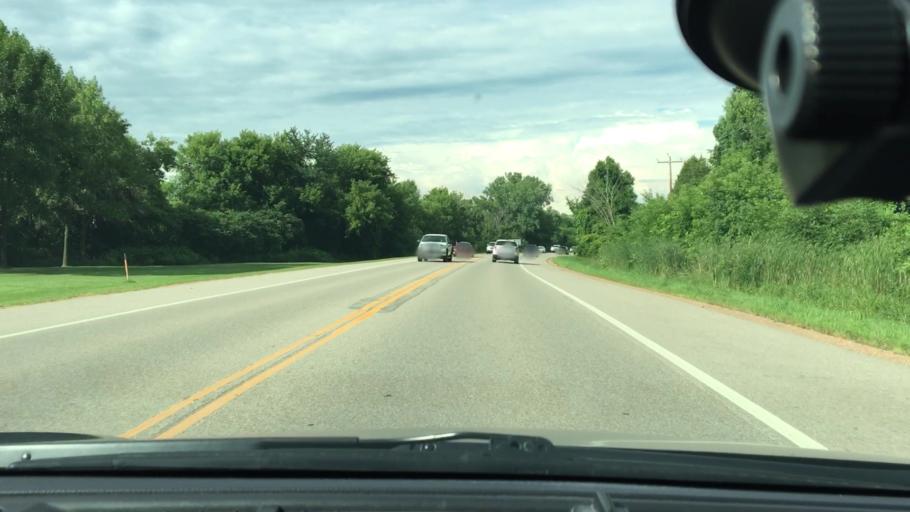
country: US
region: Minnesota
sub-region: Carver County
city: Victoria
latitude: 44.8636
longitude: -93.6530
